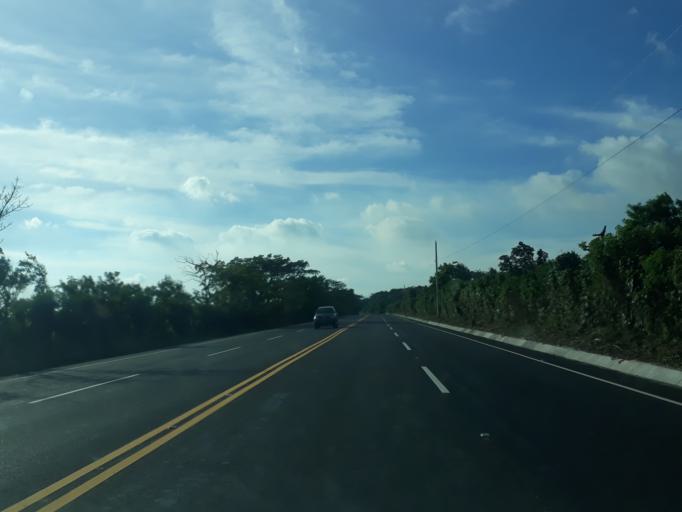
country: NI
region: Carazo
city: Diriamba
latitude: 11.9114
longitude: -86.2670
